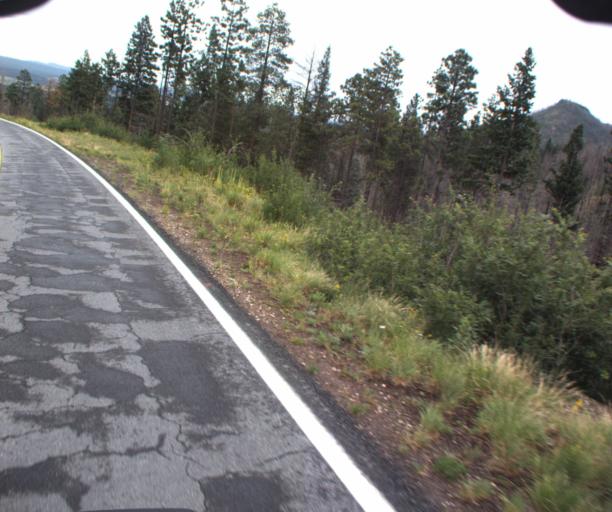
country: US
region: Arizona
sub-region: Apache County
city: Eagar
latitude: 33.8165
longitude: -109.1586
